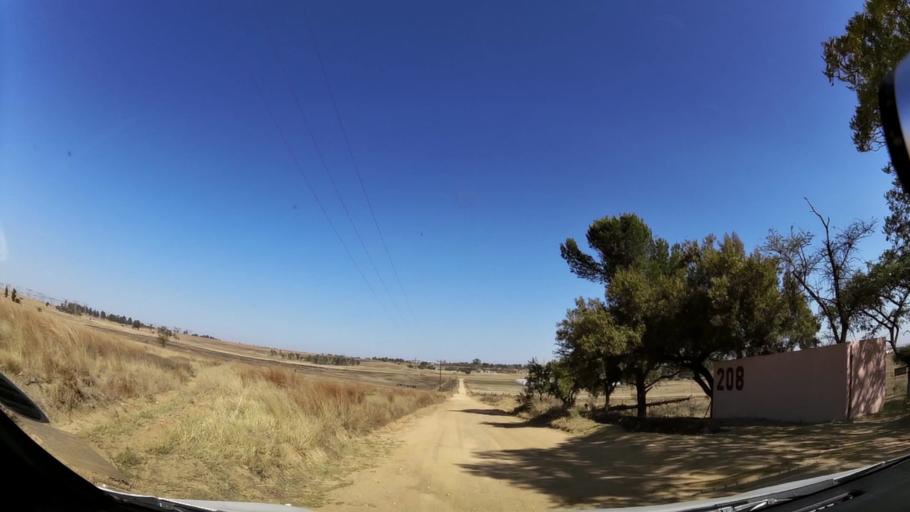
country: ZA
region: Gauteng
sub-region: City of Johannesburg Metropolitan Municipality
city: Diepsloot
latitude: -25.9030
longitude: 28.0730
